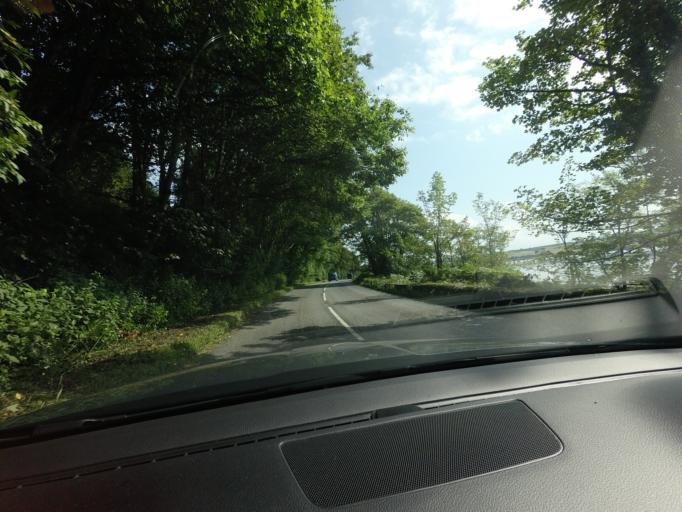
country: GB
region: Scotland
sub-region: Highland
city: Dingwall
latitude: 57.6240
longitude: -4.3799
